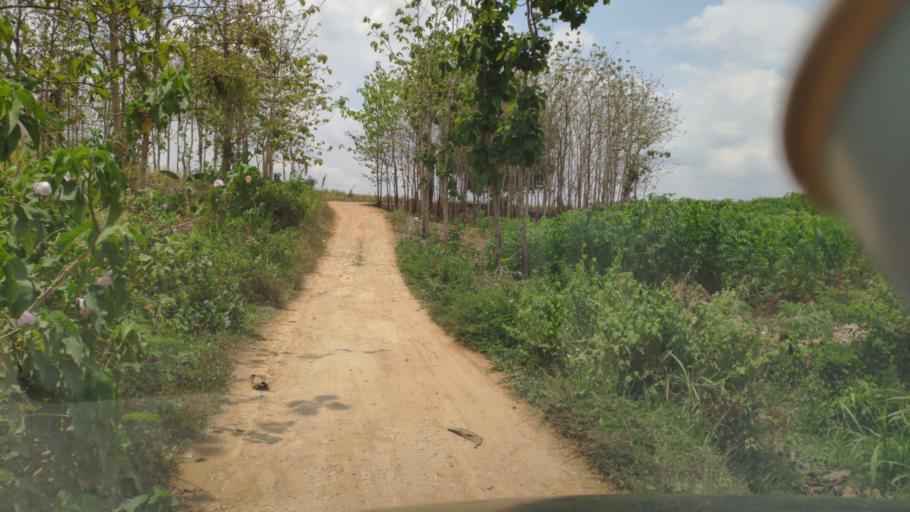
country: ID
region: Central Java
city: Ngapus
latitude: -6.9688
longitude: 111.2209
